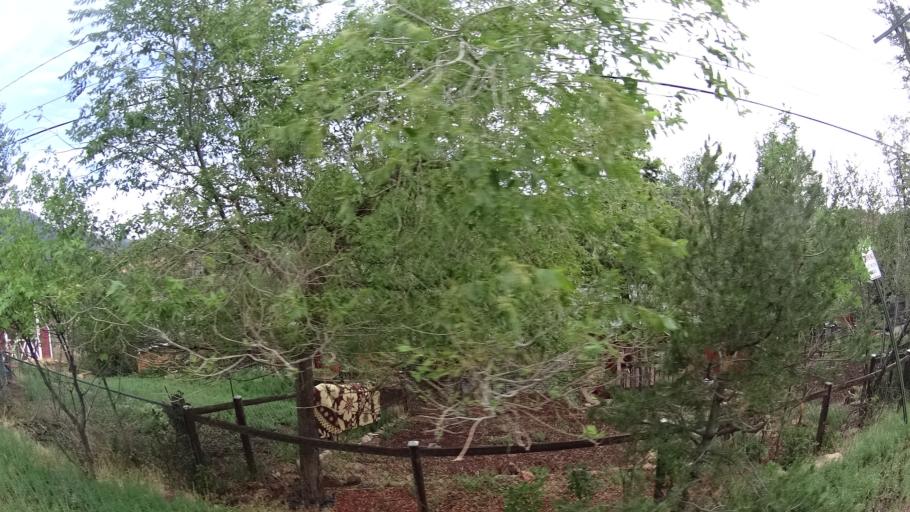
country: US
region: Colorado
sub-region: El Paso County
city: Manitou Springs
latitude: 38.8565
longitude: -104.9073
